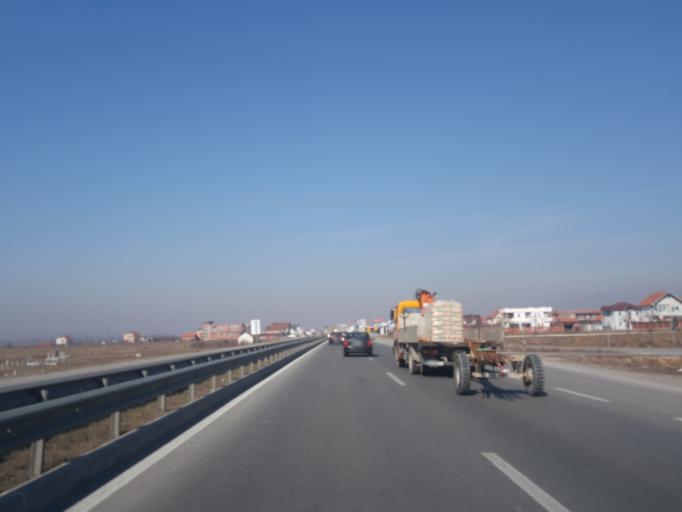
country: XK
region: Pristina
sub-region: Komuna e Obiliqit
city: Obiliq
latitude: 42.7607
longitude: 21.0307
